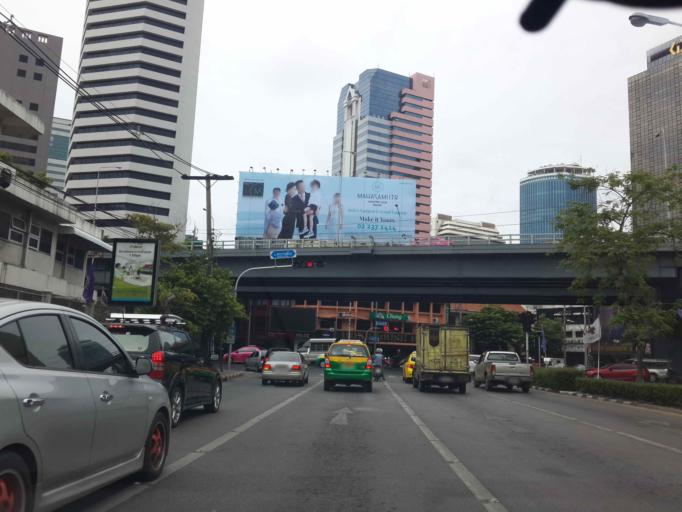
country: TH
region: Bangkok
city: Bang Rak
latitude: 13.7314
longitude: 100.5338
